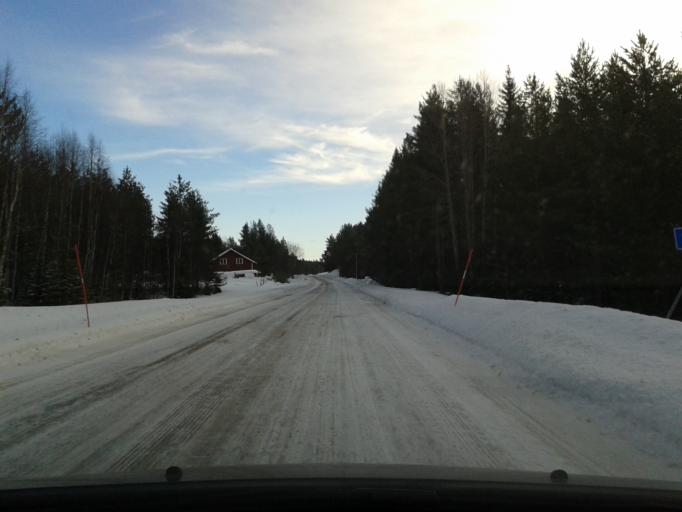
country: SE
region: Vaesterbotten
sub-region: Asele Kommun
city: Asele
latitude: 64.2268
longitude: 17.3027
